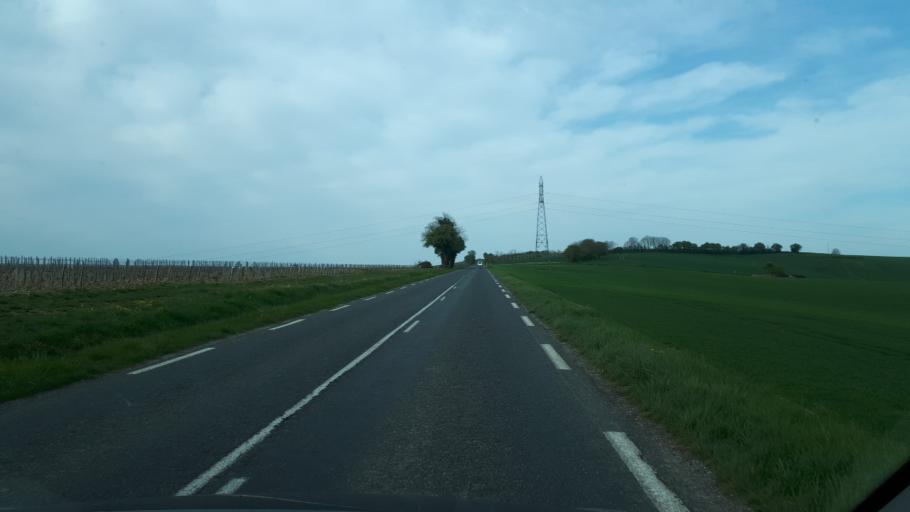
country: FR
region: Centre
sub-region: Departement du Cher
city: Sancerre
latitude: 47.2657
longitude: 2.7187
